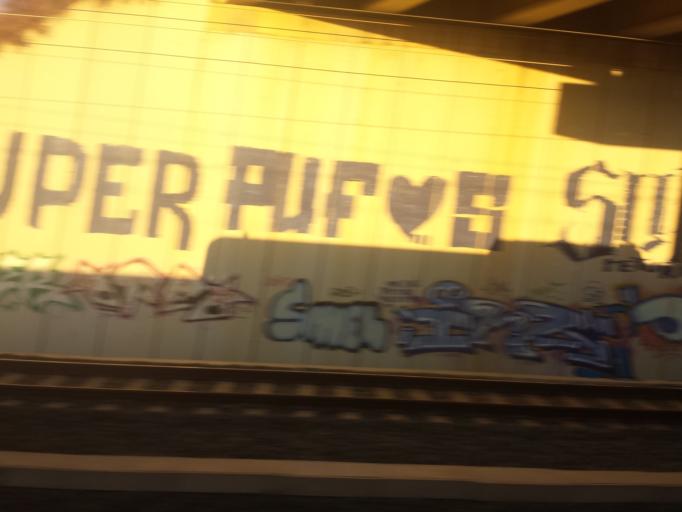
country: ES
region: Aragon
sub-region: Provincia de Zaragoza
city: Zaragoza
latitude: 41.7070
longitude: -0.8504
